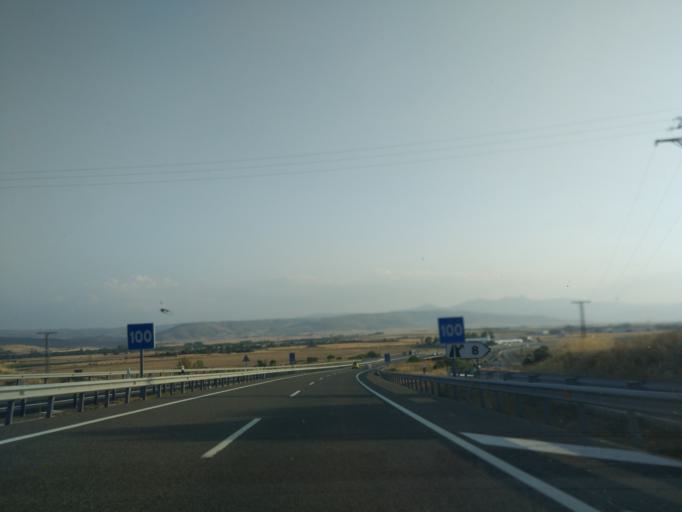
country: ES
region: Castille and Leon
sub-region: Provincia de Avila
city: Avila
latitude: 40.6514
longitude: -4.7250
